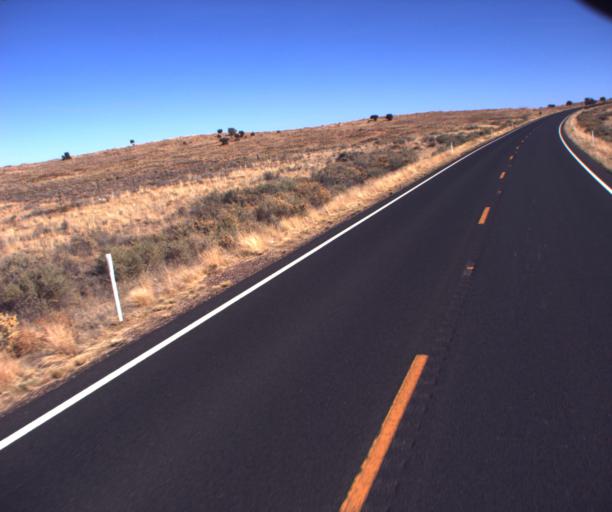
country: US
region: Arizona
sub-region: Apache County
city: Ganado
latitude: 35.7882
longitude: -109.6808
